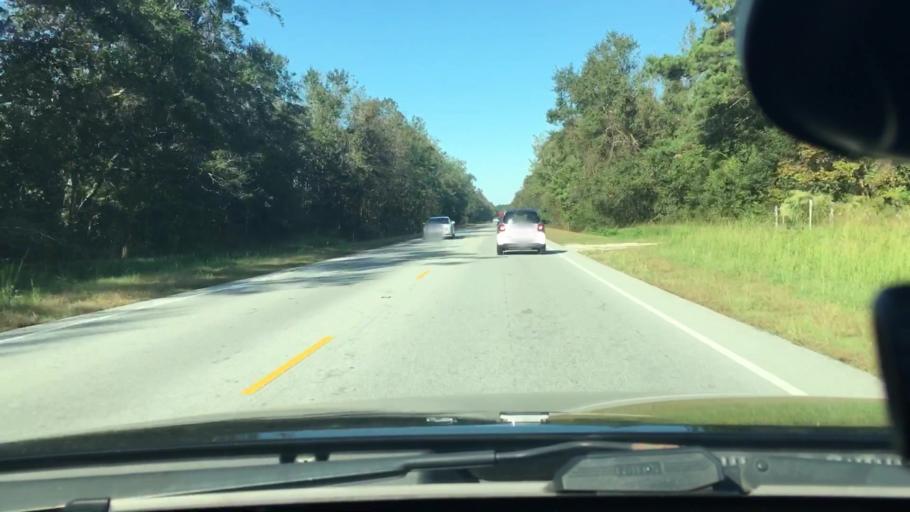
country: US
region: North Carolina
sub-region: Craven County
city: Vanceboro
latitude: 35.2004
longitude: -77.1299
